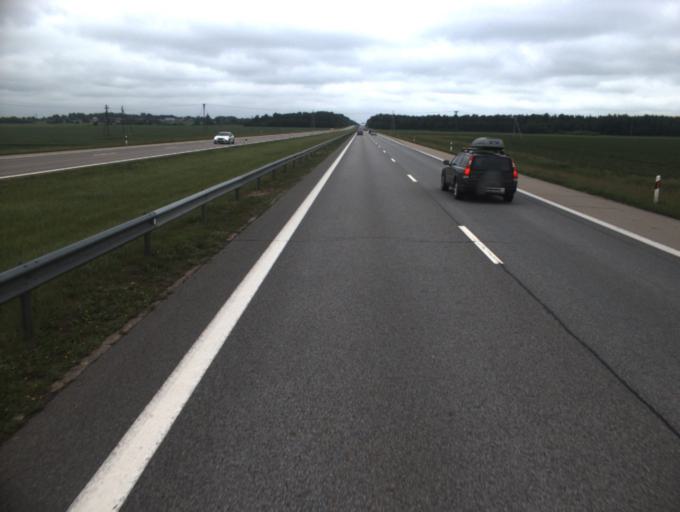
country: LT
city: Raseiniai
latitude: 55.3294
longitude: 23.1365
